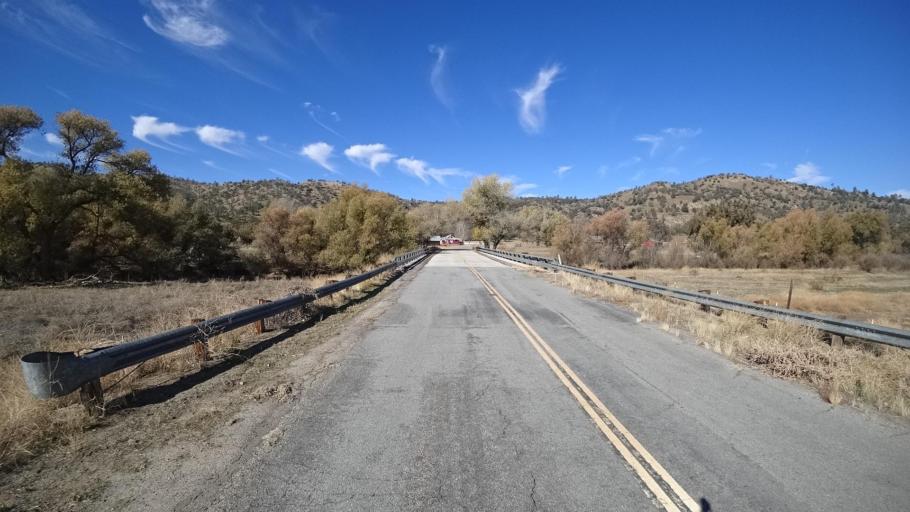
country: US
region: California
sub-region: Kern County
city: Alta Sierra
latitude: 35.6270
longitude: -118.7487
